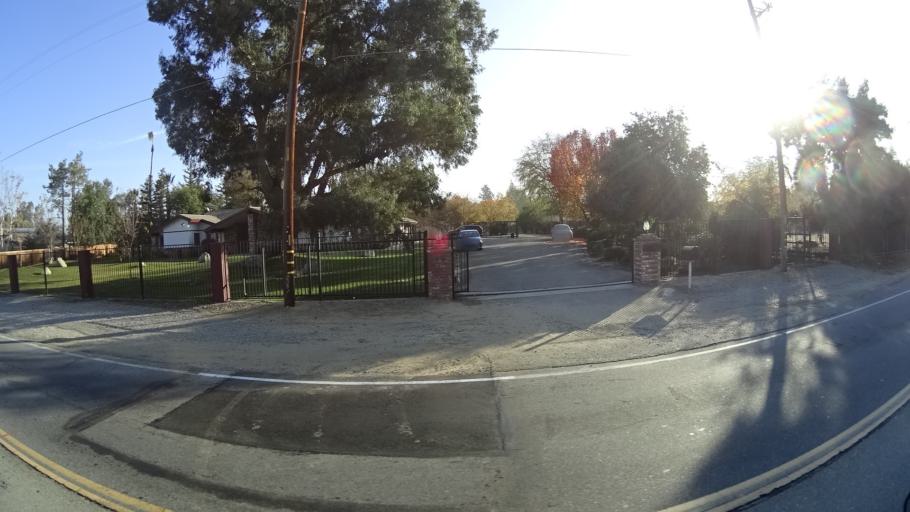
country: US
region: California
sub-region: Kern County
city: Greenacres
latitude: 35.4212
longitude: -119.0922
